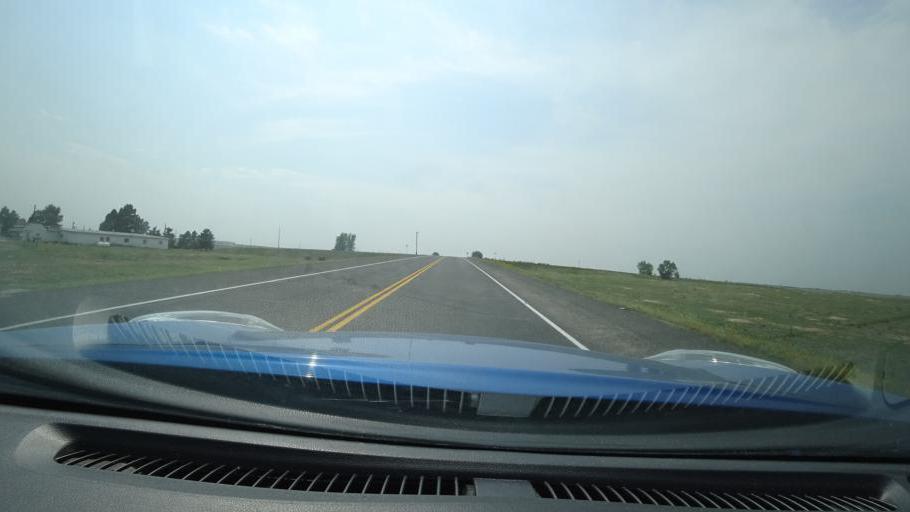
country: US
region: Colorado
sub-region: Adams County
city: Aurora
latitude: 39.7547
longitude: -104.7134
